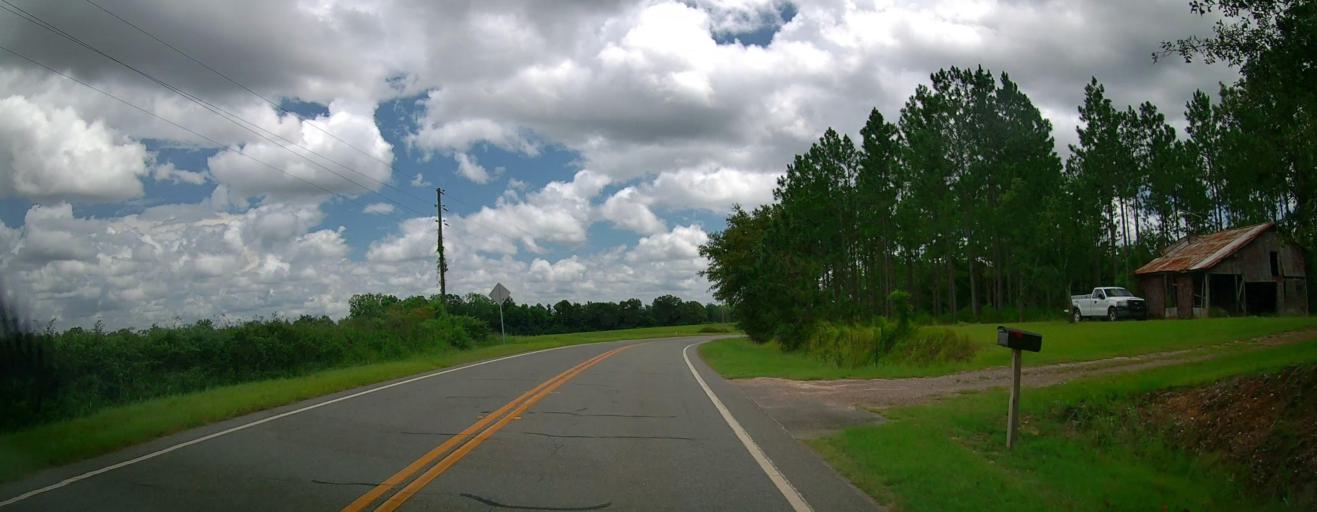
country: US
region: Georgia
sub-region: Wilcox County
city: Rochelle
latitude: 31.9929
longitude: -83.5489
